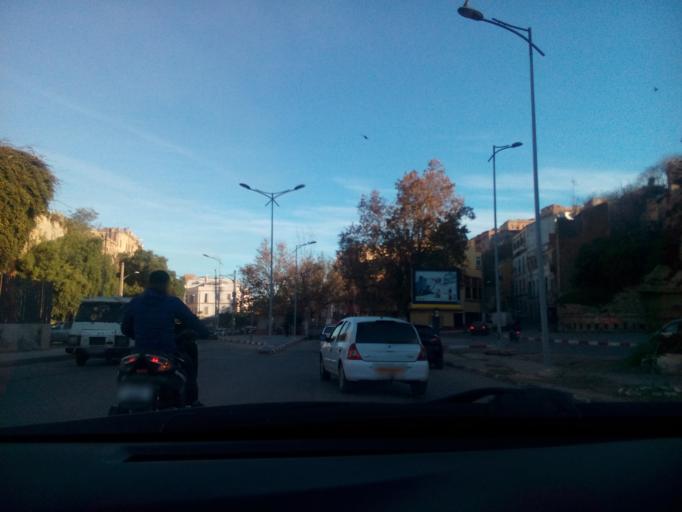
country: DZ
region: Oran
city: Oran
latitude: 35.7009
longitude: -0.6540
